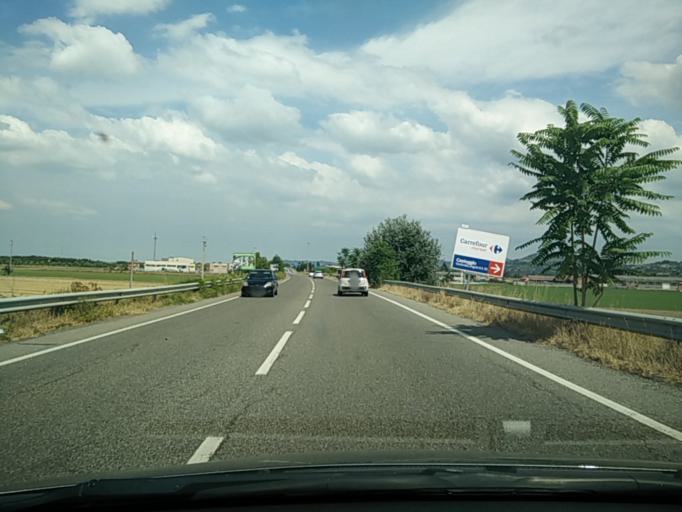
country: IT
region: Lombardy
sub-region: Provincia di Pavia
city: Verretto
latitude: 45.0302
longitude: 9.1219
